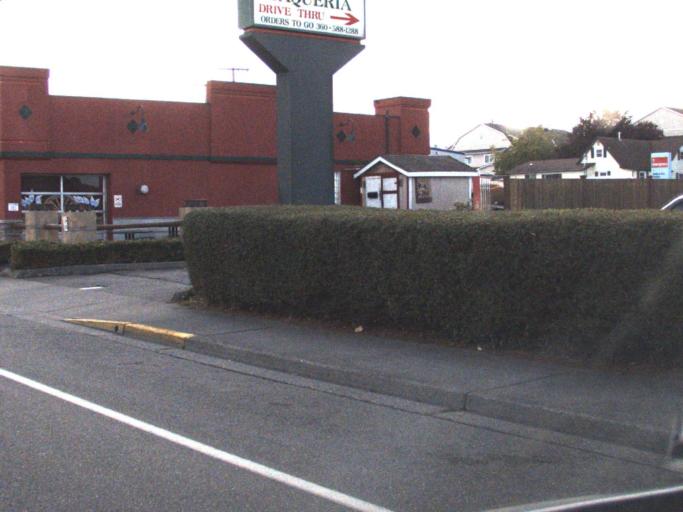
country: US
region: Washington
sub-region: Jefferson County
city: Port Hadlock-Irondale
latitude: 48.0082
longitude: -122.8325
